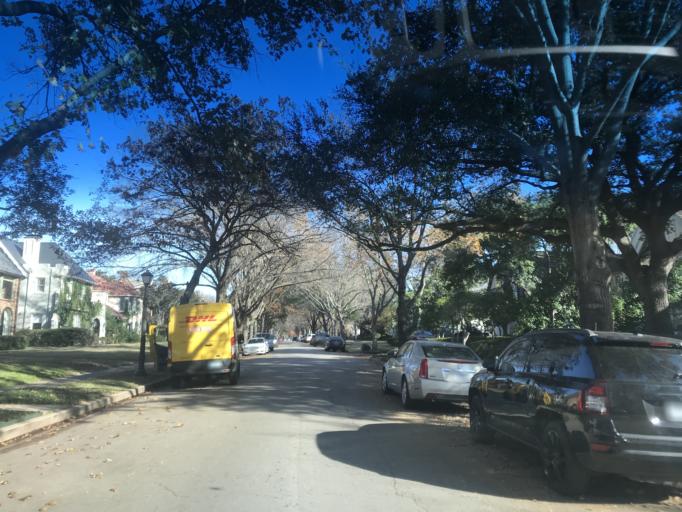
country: US
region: Texas
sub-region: Dallas County
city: Highland Park
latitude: 32.8238
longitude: -96.8116
